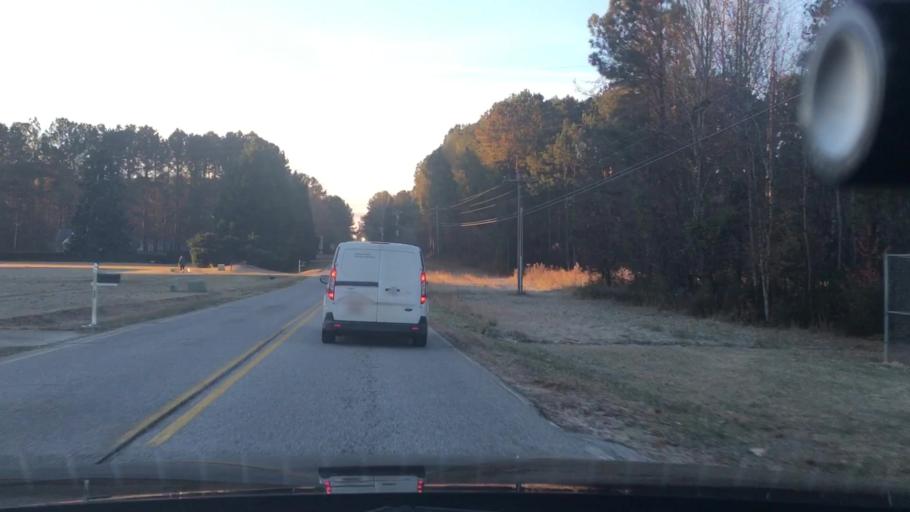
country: US
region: Georgia
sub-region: Coweta County
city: East Newnan
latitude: 33.3906
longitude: -84.7014
